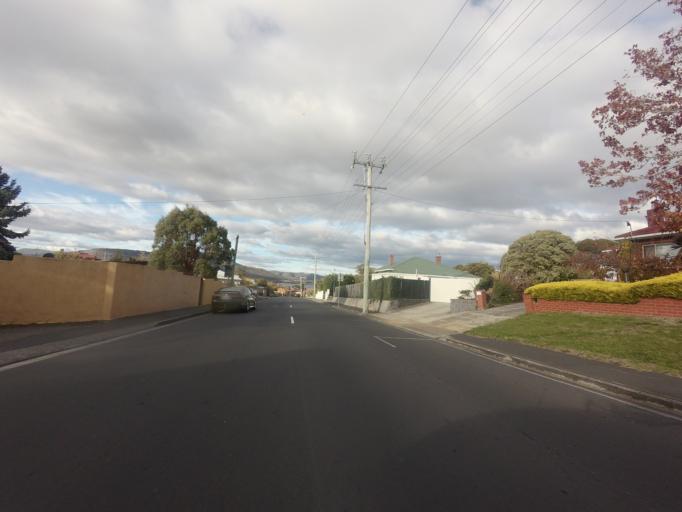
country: AU
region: Tasmania
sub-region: Glenorchy
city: Berriedale
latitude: -42.8230
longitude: 147.2583
